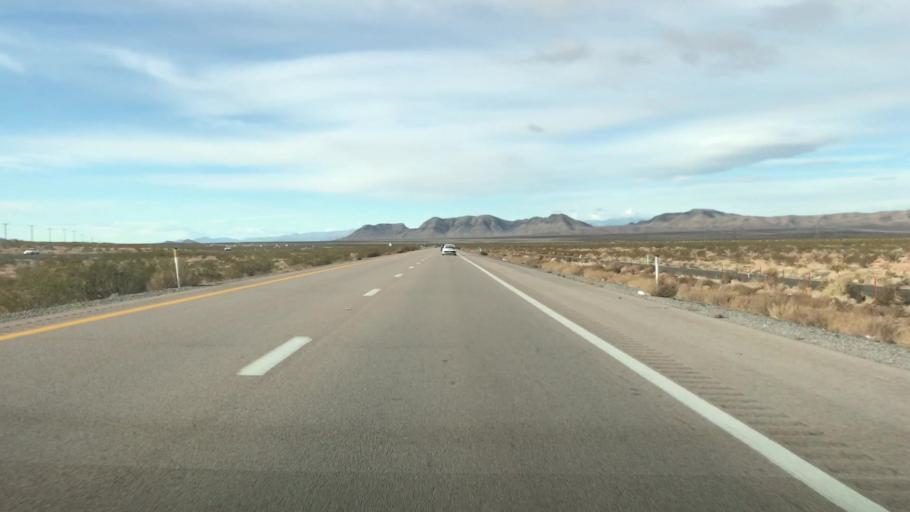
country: US
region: Nevada
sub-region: Clark County
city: Moapa Valley
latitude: 36.7479
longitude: -114.4114
